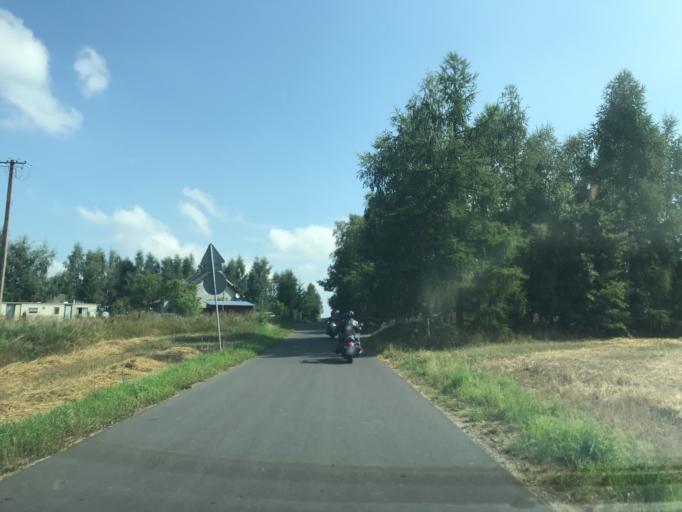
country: PL
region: Warmian-Masurian Voivodeship
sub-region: Powiat nowomiejski
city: Biskupiec
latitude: 53.4541
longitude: 19.4540
